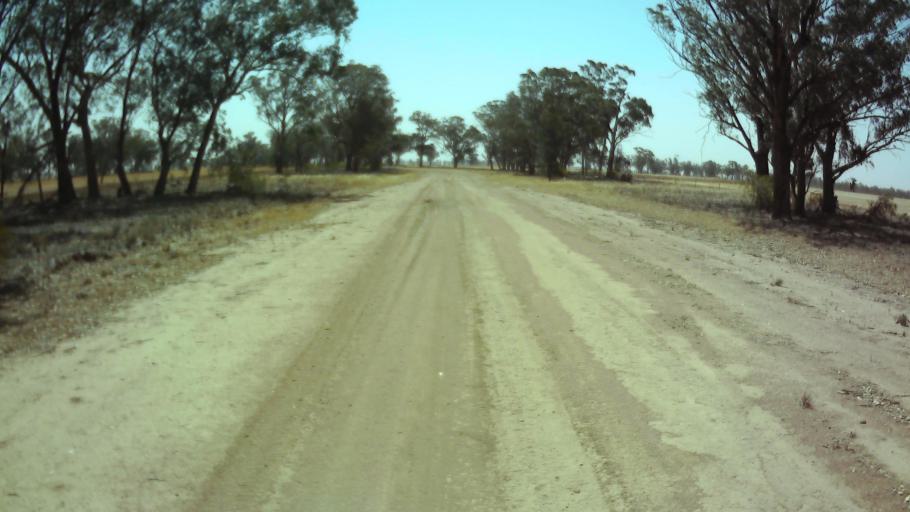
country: AU
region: New South Wales
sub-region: Weddin
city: Grenfell
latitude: -33.9371
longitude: 147.8076
